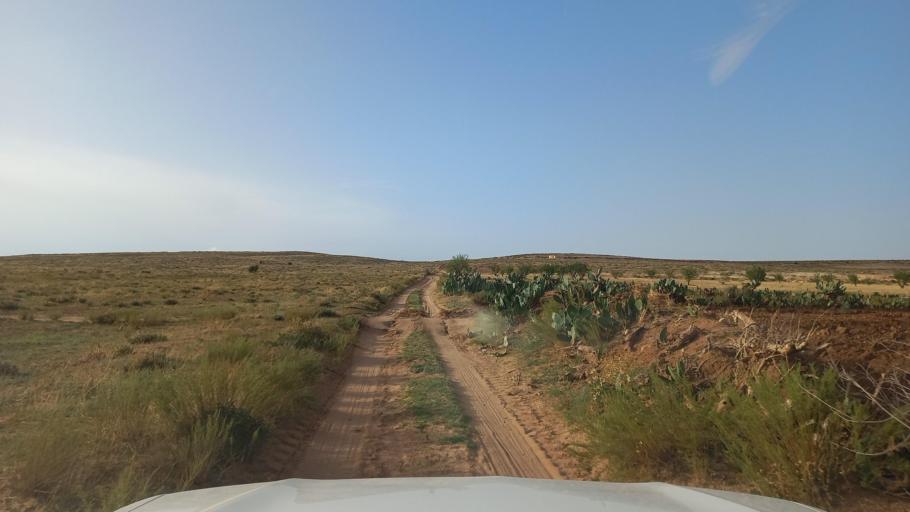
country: TN
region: Al Qasrayn
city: Kasserine
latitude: 35.3587
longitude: 8.8410
